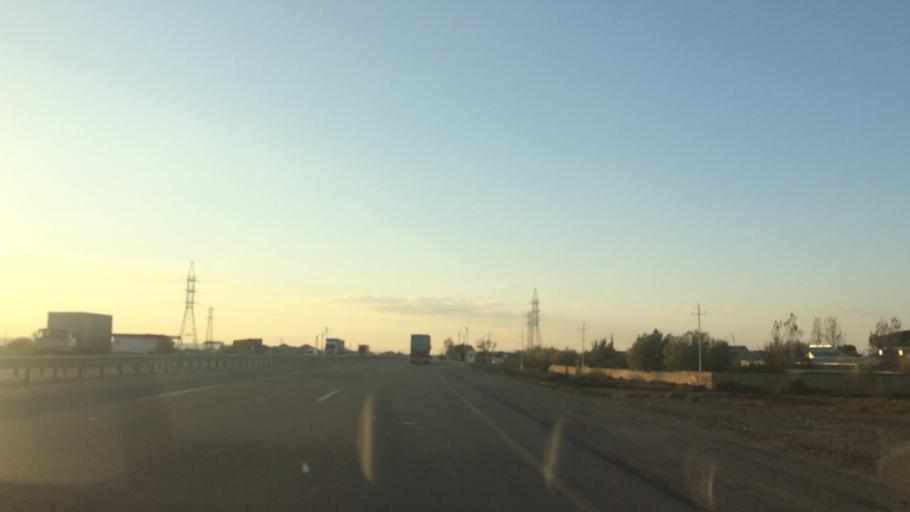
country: AZ
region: Baki
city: Qobustan
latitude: 39.9690
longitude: 49.2689
